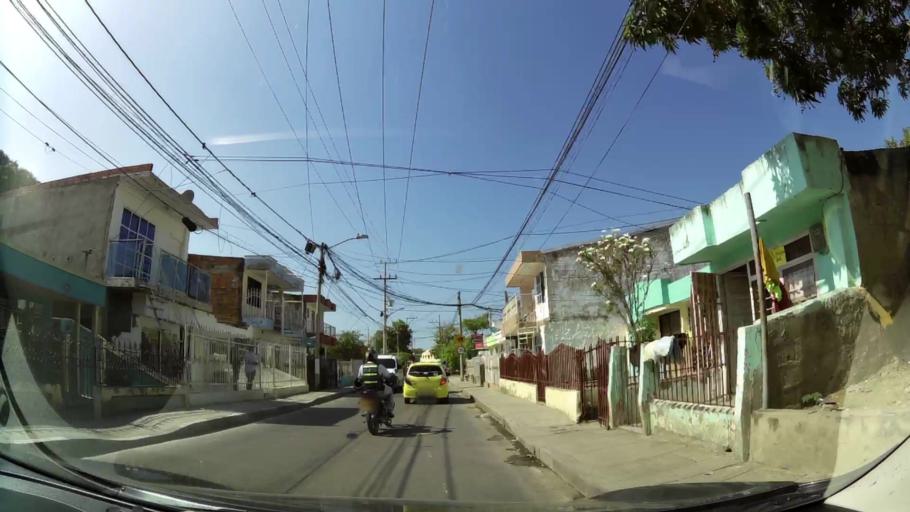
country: CO
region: Bolivar
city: Cartagena
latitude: 10.3793
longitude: -75.4699
